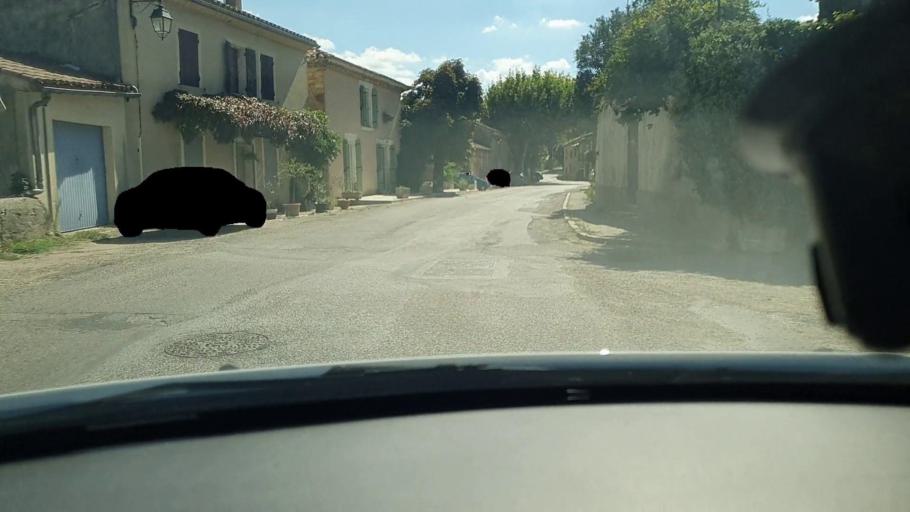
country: FR
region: Languedoc-Roussillon
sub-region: Departement du Gard
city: Goudargues
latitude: 44.1625
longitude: 4.4860
